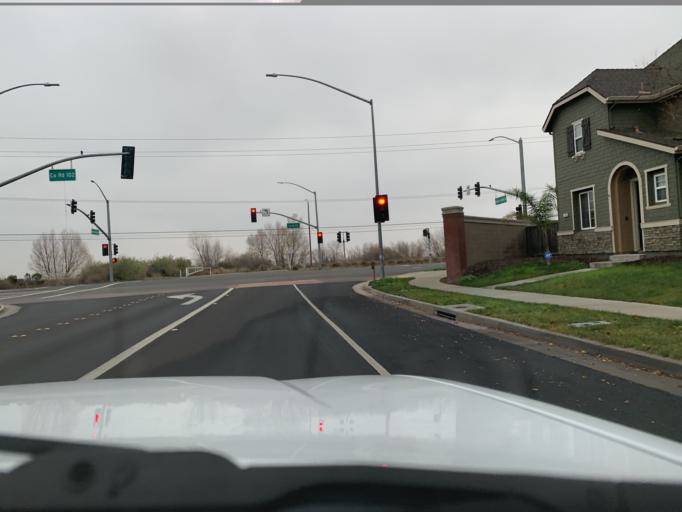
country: US
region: California
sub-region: Yolo County
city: Woodland
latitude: 38.6548
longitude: -121.7294
